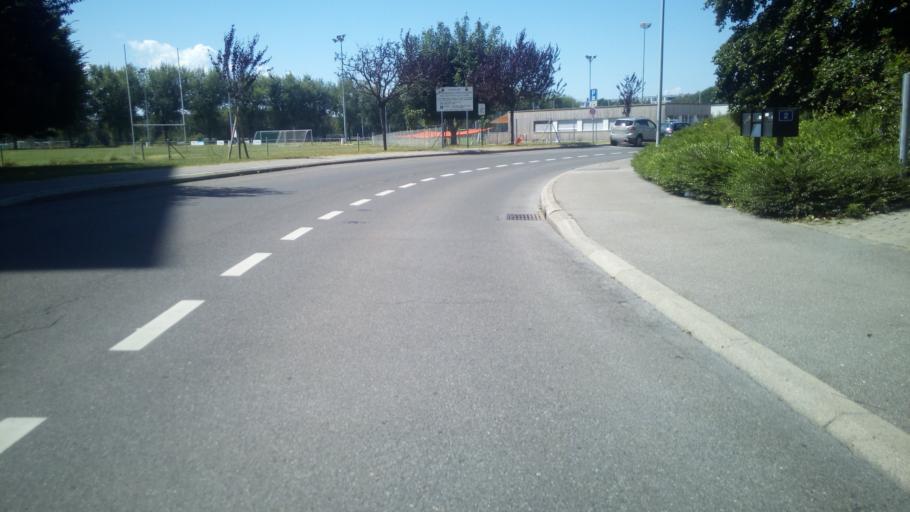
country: CH
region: Vaud
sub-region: Ouest Lausannois District
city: Chavannes
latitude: 46.5263
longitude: 6.5728
